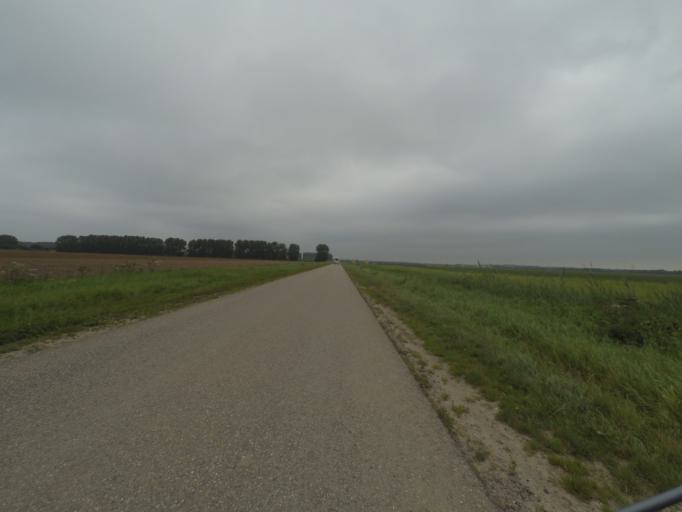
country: NL
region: Flevoland
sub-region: Gemeente Lelystad
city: Lelystad
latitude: 52.4774
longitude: 5.4632
